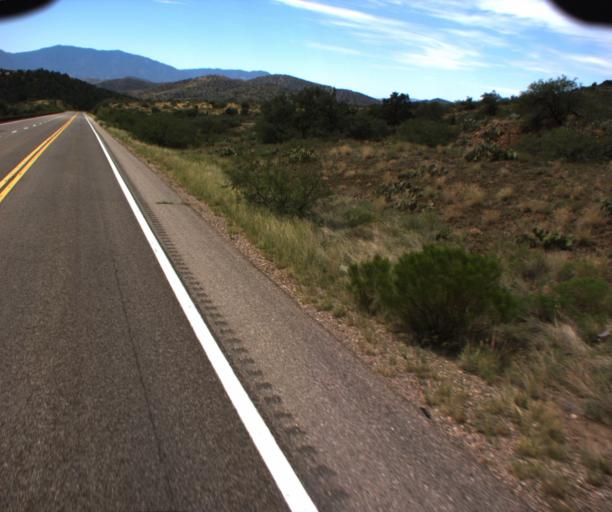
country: US
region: Arizona
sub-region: Gila County
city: Globe
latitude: 33.5032
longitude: -110.7077
